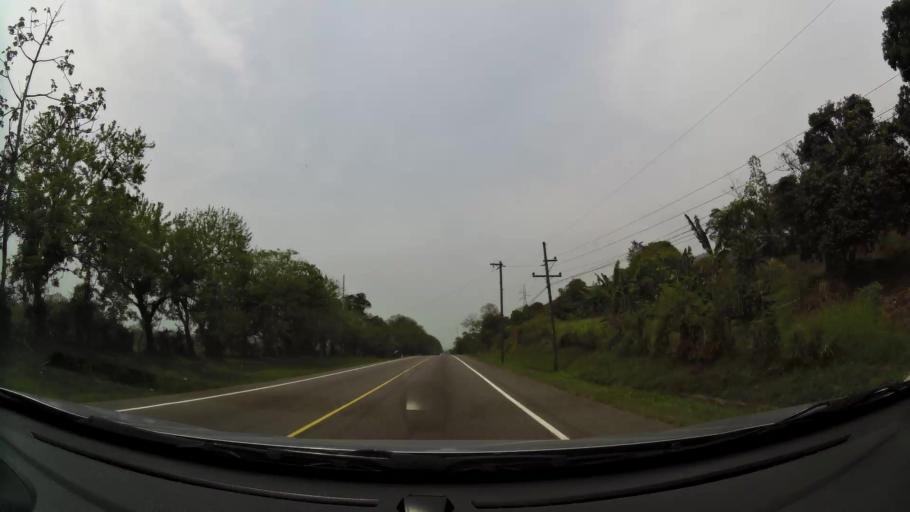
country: HN
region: Cortes
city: La Guama
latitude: 14.8330
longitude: -87.9603
